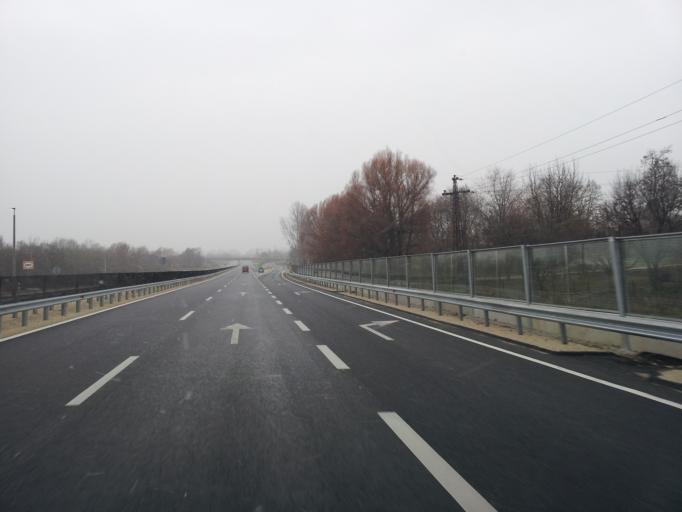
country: HU
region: Veszprem
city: Herend
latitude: 47.1294
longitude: 17.7562
